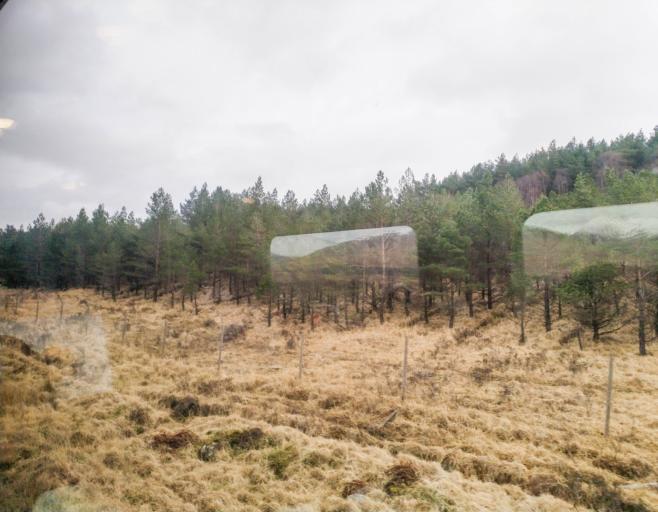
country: GB
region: Scotland
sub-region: Highland
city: Spean Bridge
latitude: 56.5344
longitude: -4.7629
